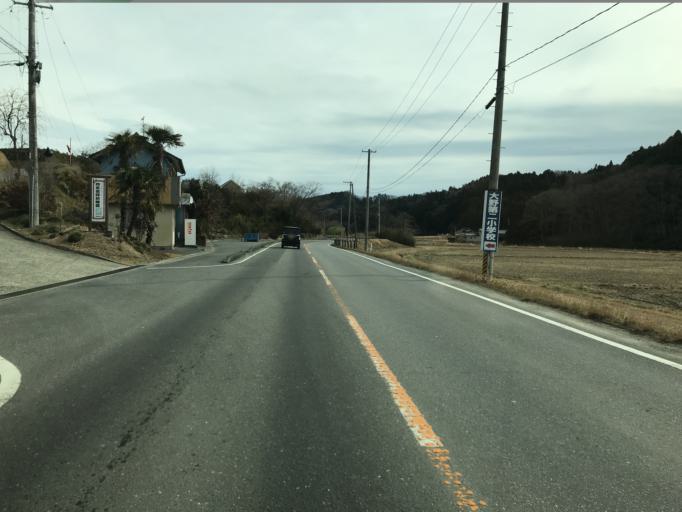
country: JP
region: Fukushima
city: Iwaki
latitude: 37.1133
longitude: 140.9014
